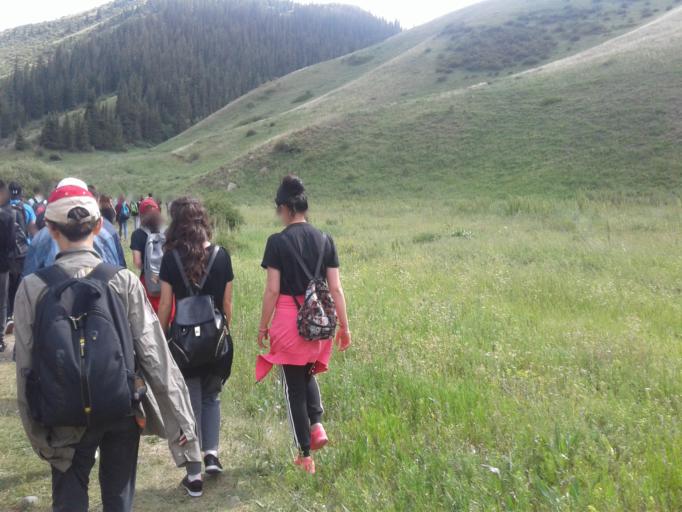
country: KG
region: Naryn
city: Naryn
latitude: 41.4585
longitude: 76.4530
